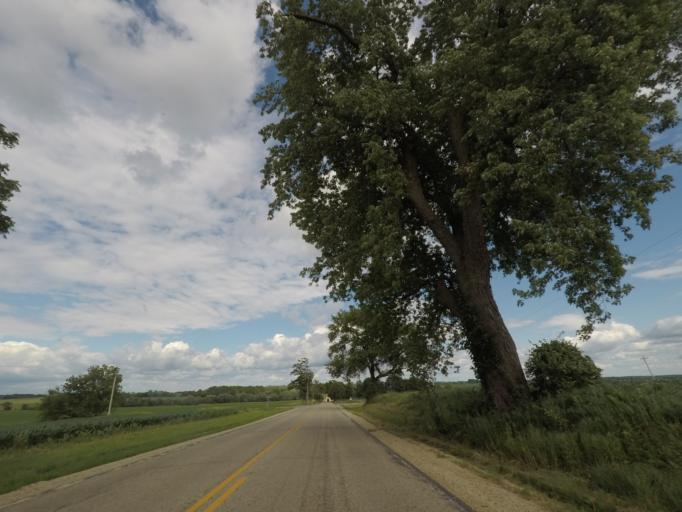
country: US
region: Wisconsin
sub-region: Rock County
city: Orfordville
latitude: 42.7113
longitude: -89.2015
